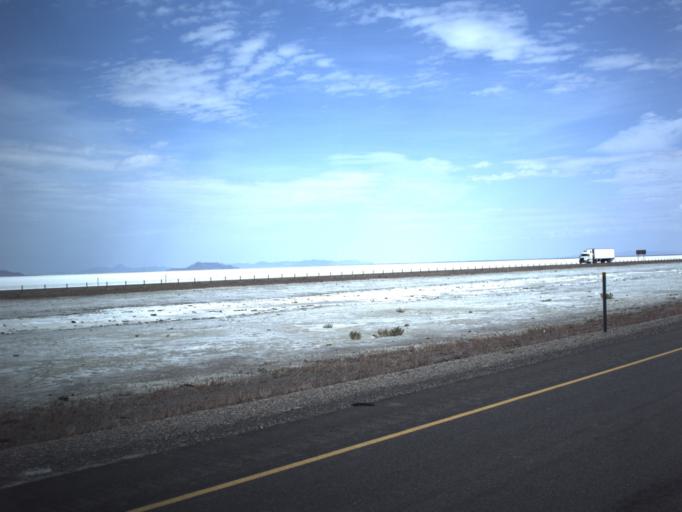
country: US
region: Utah
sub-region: Tooele County
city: Wendover
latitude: 40.7389
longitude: -113.8736
